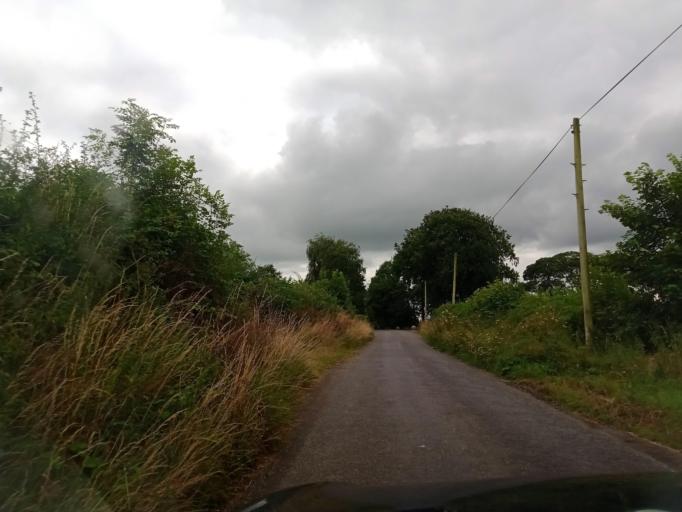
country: IE
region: Leinster
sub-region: Laois
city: Stradbally
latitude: 52.9770
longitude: -7.1600
